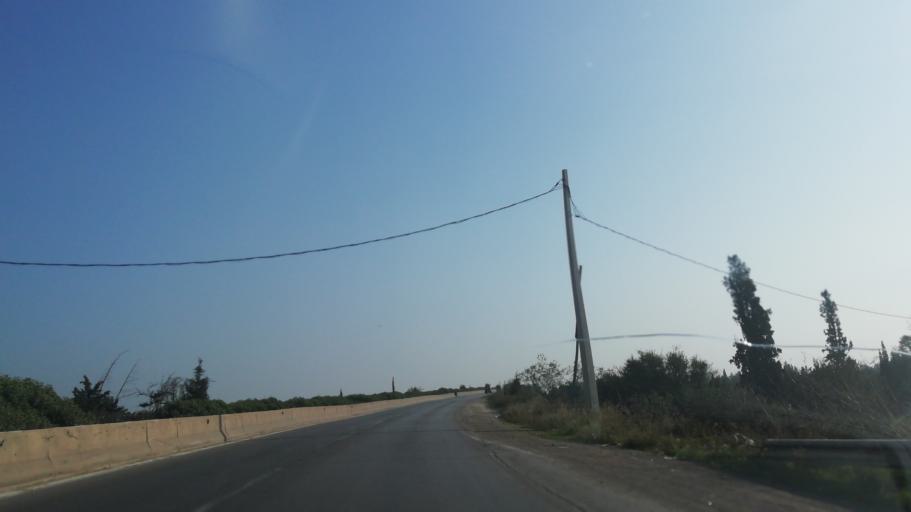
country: DZ
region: Oran
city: Bou Tlelis
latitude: 35.5680
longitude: -0.9094
